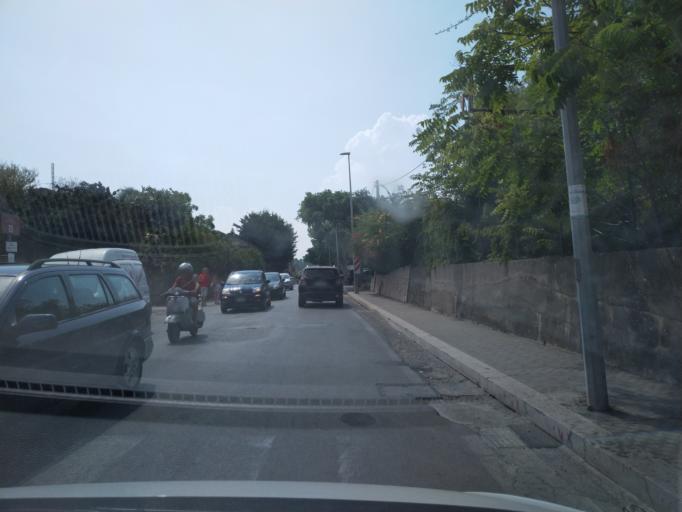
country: IT
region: Sicily
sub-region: Palermo
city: Cefalu
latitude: 38.0326
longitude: 14.0141
